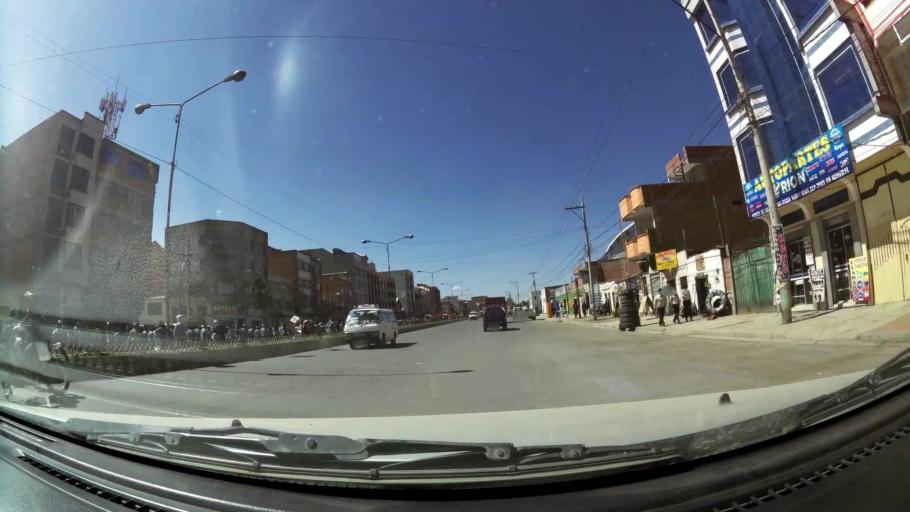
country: BO
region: La Paz
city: La Paz
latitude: -16.4978
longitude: -68.1830
